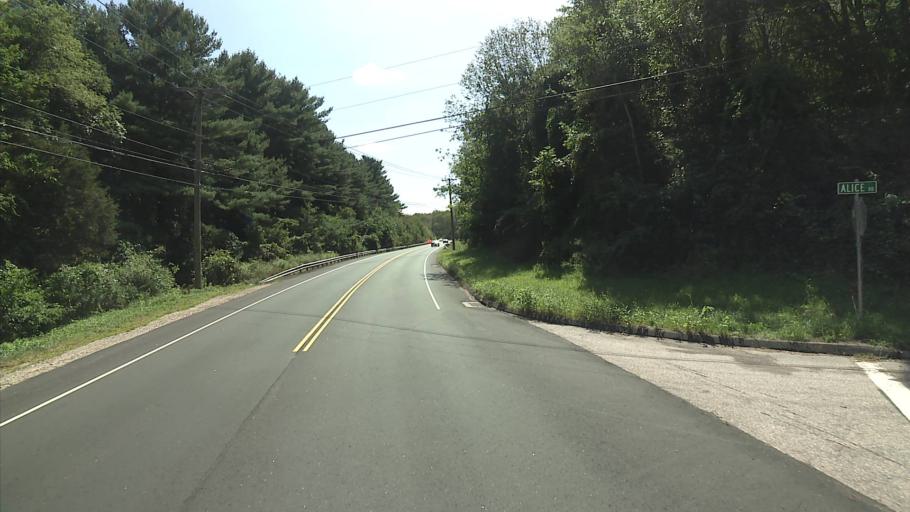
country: US
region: Connecticut
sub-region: New London County
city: Jewett City
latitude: 41.5814
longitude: -71.8951
